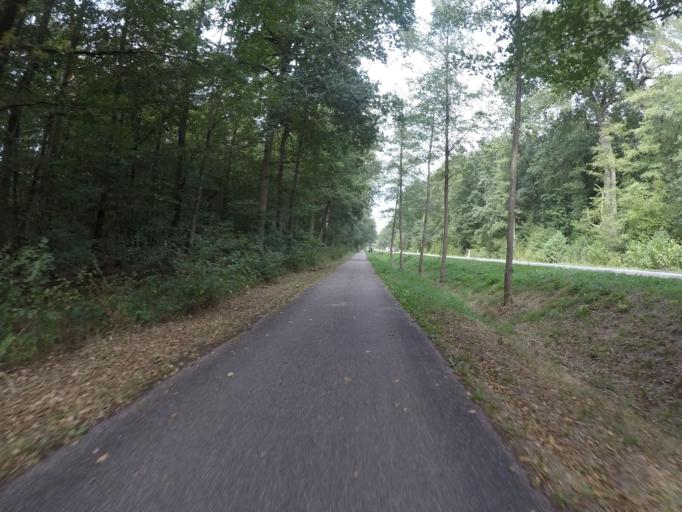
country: DE
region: Rheinland-Pfalz
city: Hanhofen
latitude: 49.3514
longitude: 8.3500
